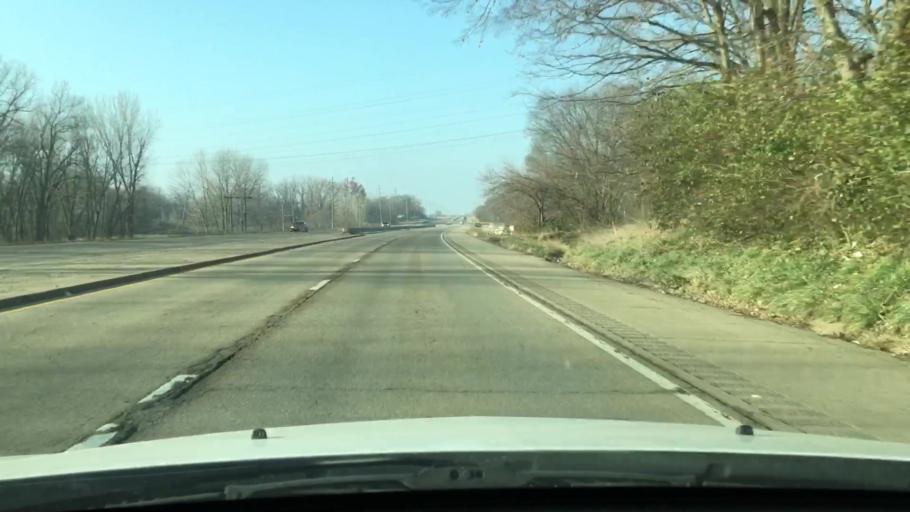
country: US
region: Illinois
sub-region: Tazewell County
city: Pekin
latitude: 40.5838
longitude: -89.6884
